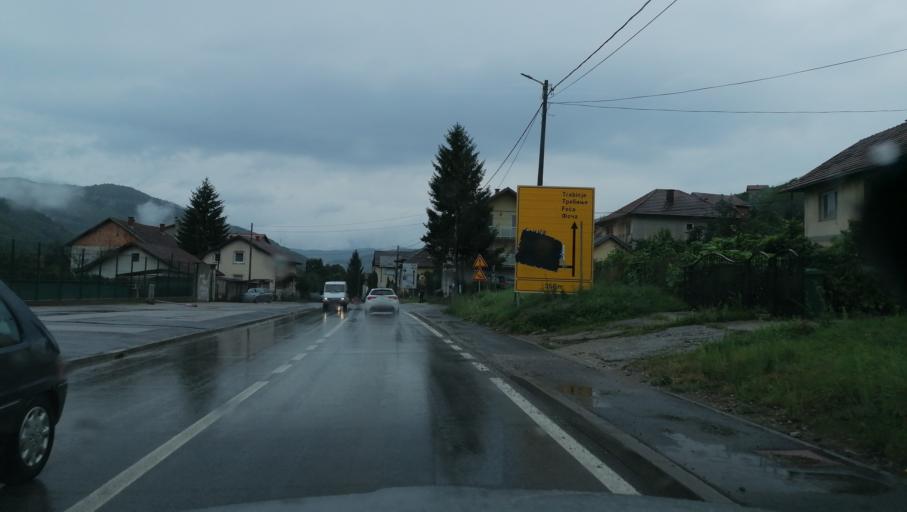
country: BA
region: Federation of Bosnia and Herzegovina
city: Gorazde
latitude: 43.6728
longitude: 18.9824
